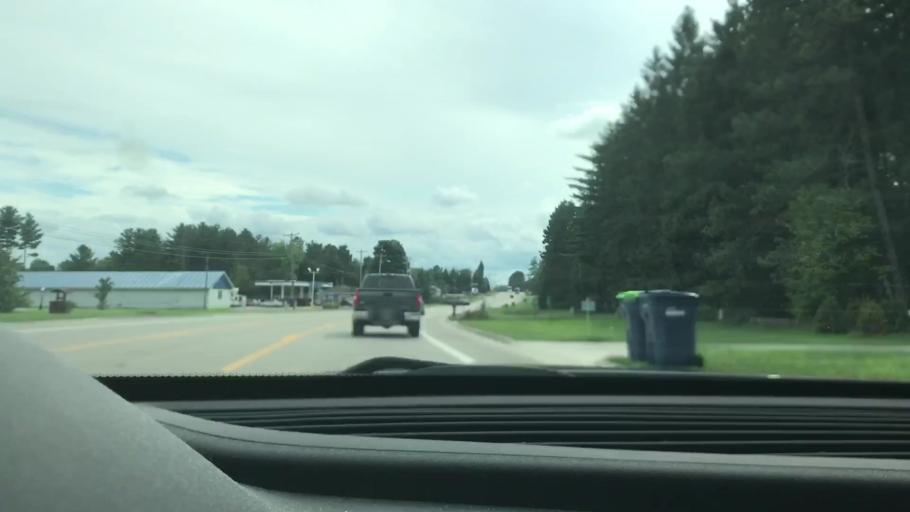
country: US
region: Michigan
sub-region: Missaukee County
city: Lake City
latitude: 44.3199
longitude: -85.2120
